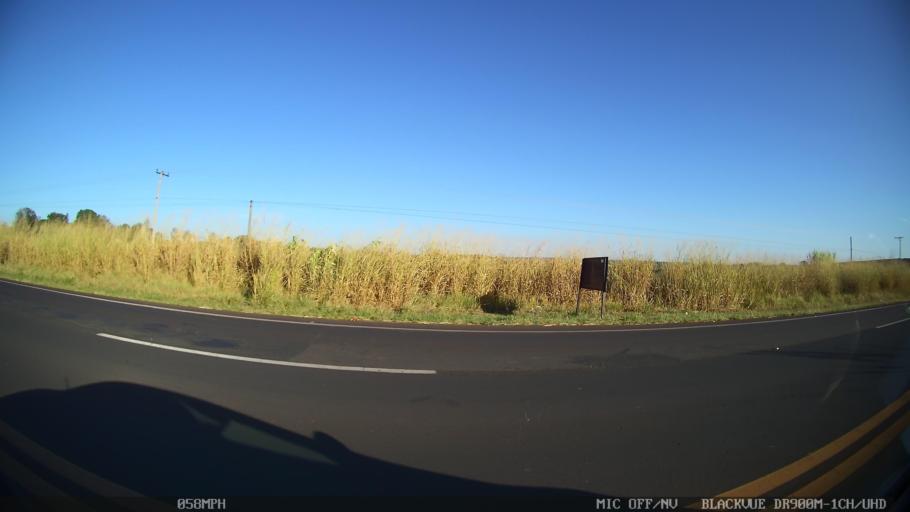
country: BR
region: Sao Paulo
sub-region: Guapiacu
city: Guapiacu
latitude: -20.7658
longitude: -49.1962
